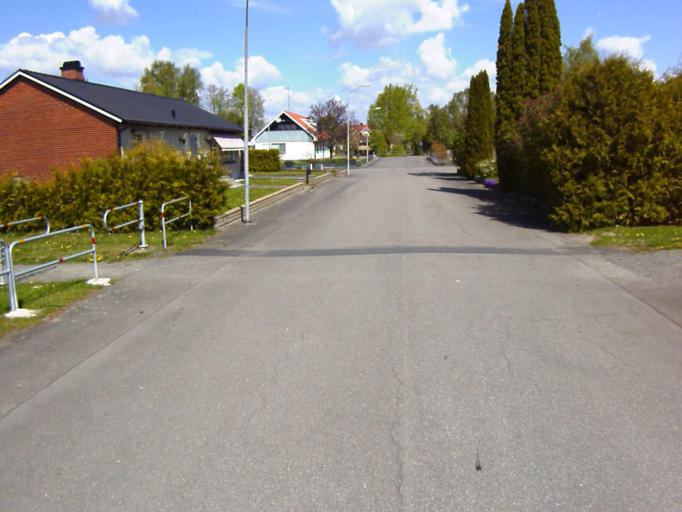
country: SE
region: Skane
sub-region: Kristianstads Kommun
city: Fjalkinge
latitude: 56.0141
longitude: 14.2298
